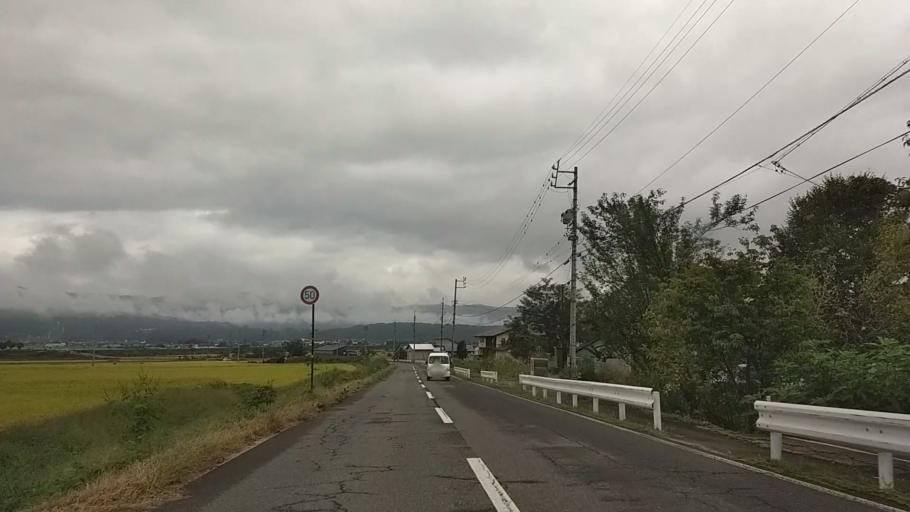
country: JP
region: Nagano
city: Iiyama
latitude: 36.8458
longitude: 138.4020
